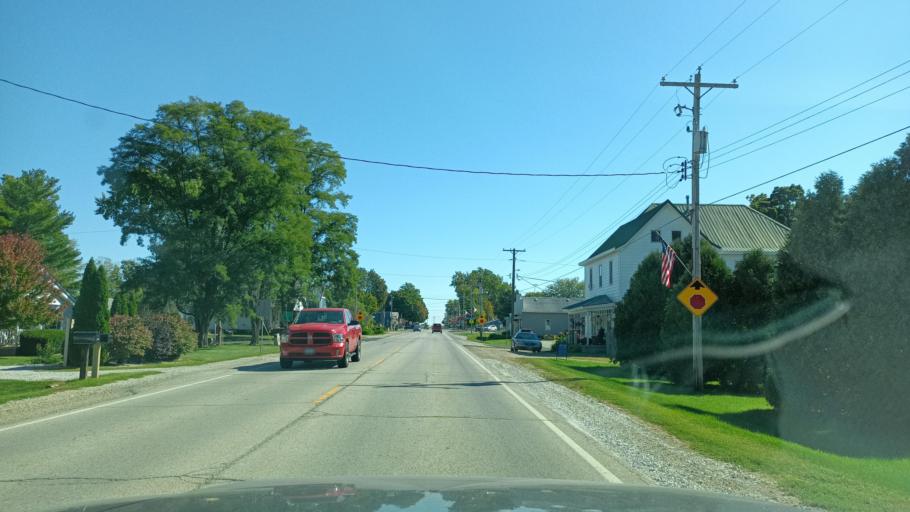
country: US
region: Illinois
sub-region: Peoria County
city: Dunlap
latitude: 40.7899
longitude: -89.7536
